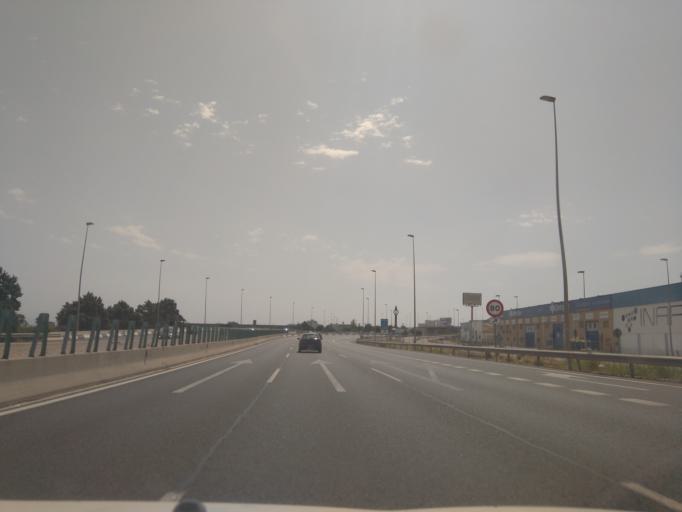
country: ES
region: Valencia
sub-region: Provincia de Valencia
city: Beniparrell
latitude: 39.3811
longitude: -0.4000
